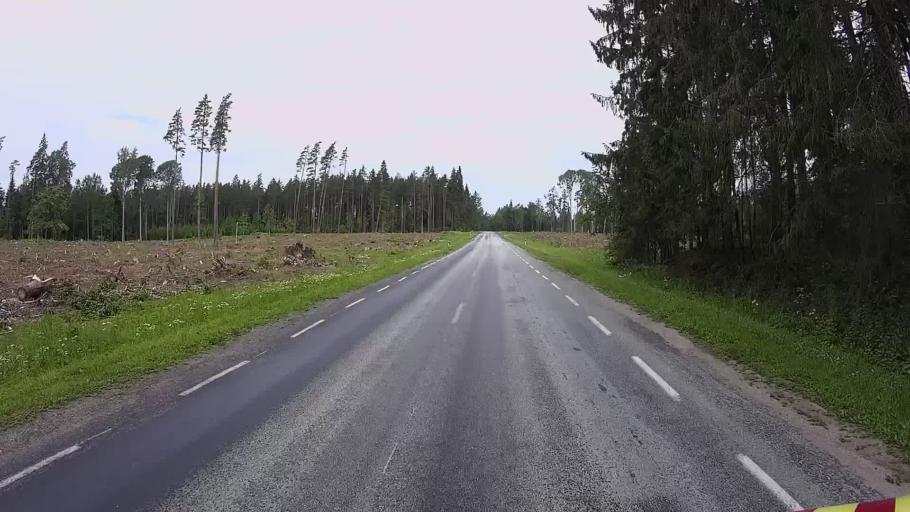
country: EE
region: Viljandimaa
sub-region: Karksi vald
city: Karksi-Nuia
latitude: 58.2192
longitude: 25.6181
